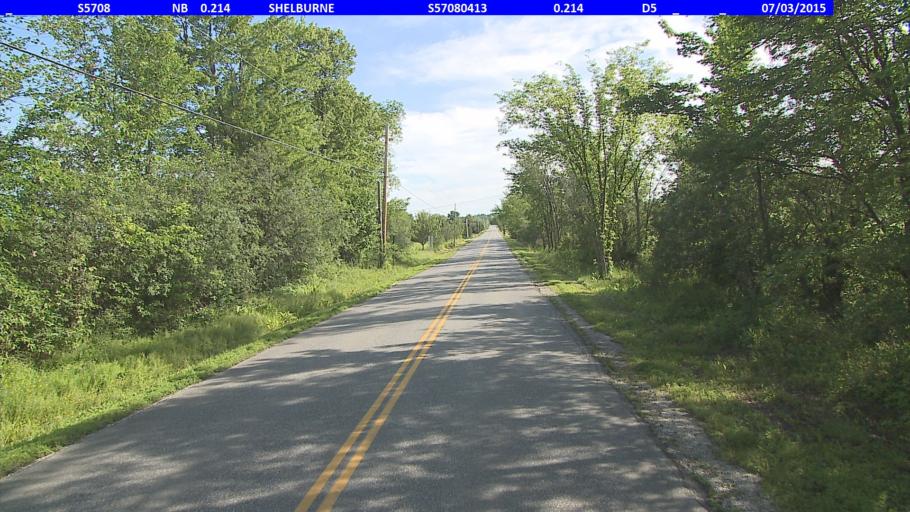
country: US
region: Vermont
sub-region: Chittenden County
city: South Burlington
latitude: 44.4105
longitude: -73.1770
